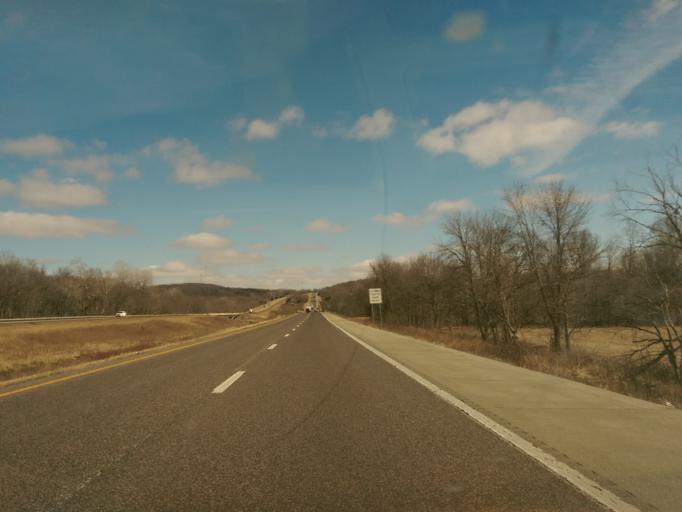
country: US
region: Missouri
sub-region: Montgomery County
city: Montgomery City
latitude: 38.8992
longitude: -91.5869
